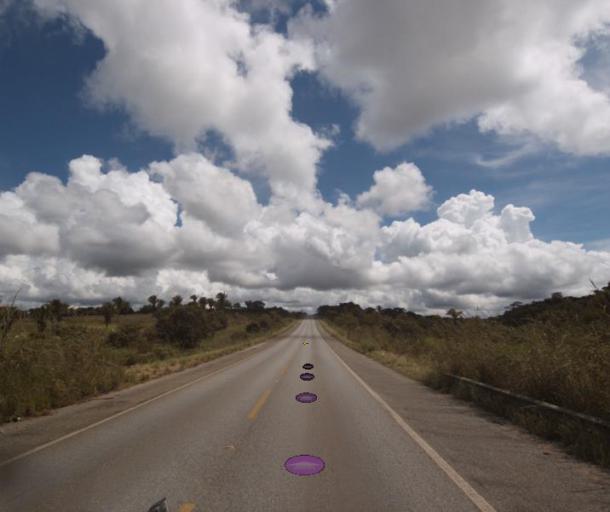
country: BR
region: Goias
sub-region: Pirenopolis
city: Pirenopolis
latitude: -15.7509
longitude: -48.6282
